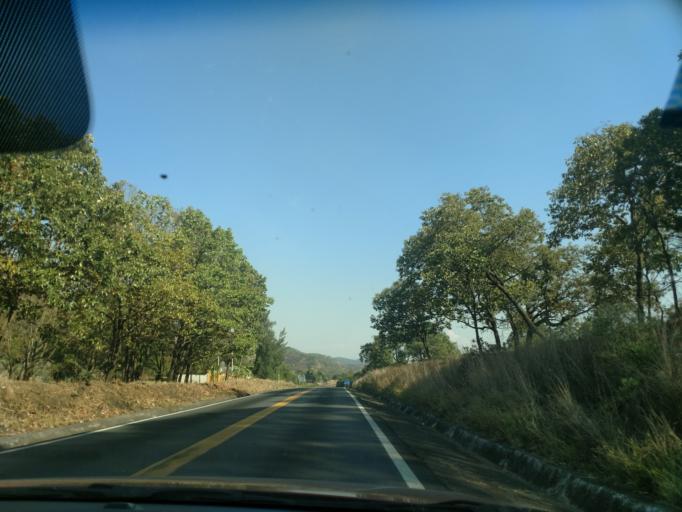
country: MX
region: Nayarit
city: Santa Maria del Oro
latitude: 21.2710
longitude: -104.6477
